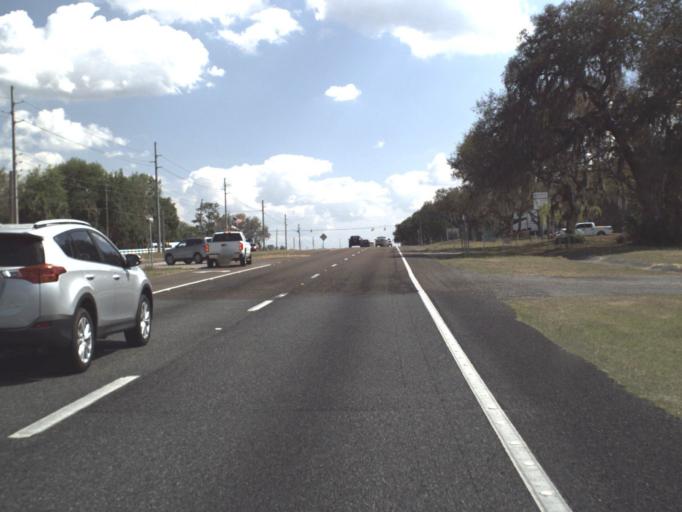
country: US
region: Florida
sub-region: Lake County
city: Hawthorne
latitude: 28.7609
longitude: -81.8799
